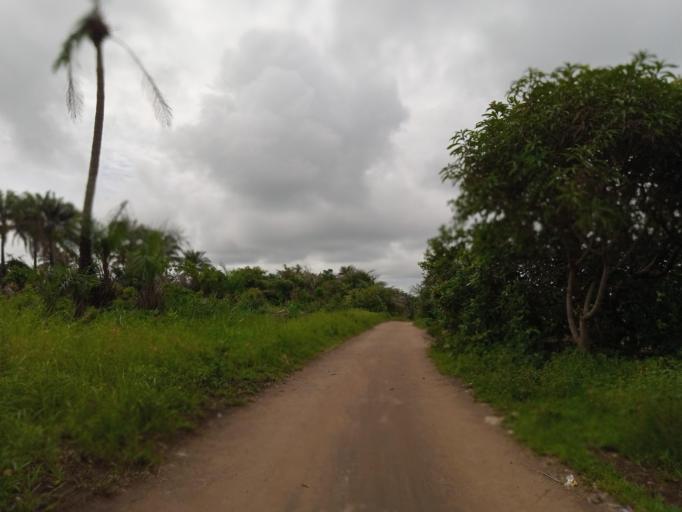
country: SL
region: Northern Province
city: Masoyila
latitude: 8.5836
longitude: -13.1926
